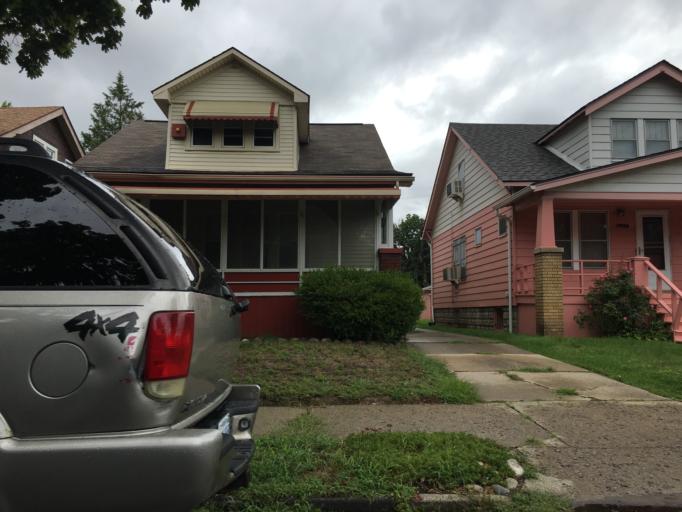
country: US
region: Michigan
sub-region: Wayne County
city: Highland Park
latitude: 42.4057
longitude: -83.1437
